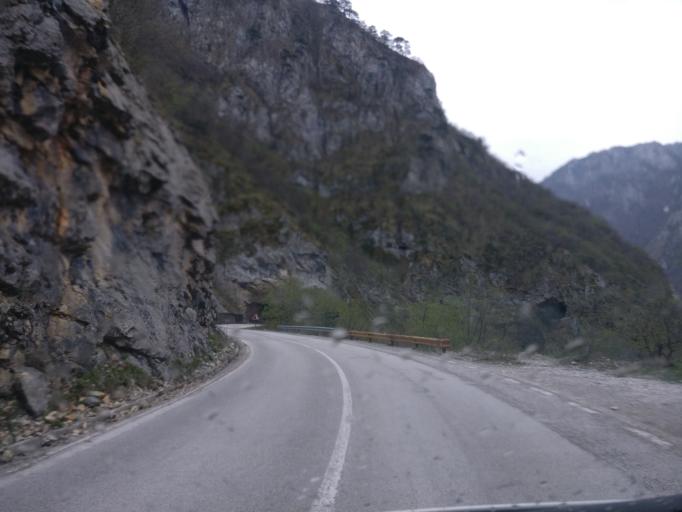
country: ME
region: Opstina Pluzine
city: Pluzine
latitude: 43.2289
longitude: 18.8468
